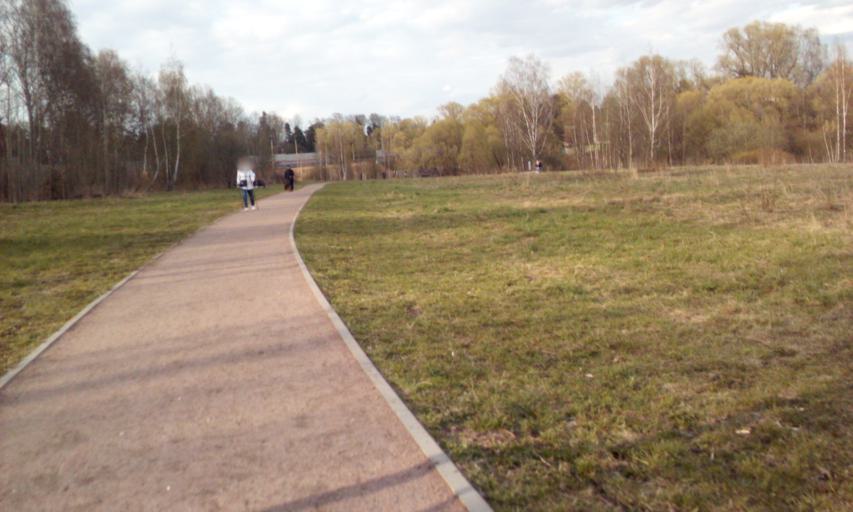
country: RU
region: Moscow
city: Novo-Peredelkino
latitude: 55.6499
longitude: 37.3352
